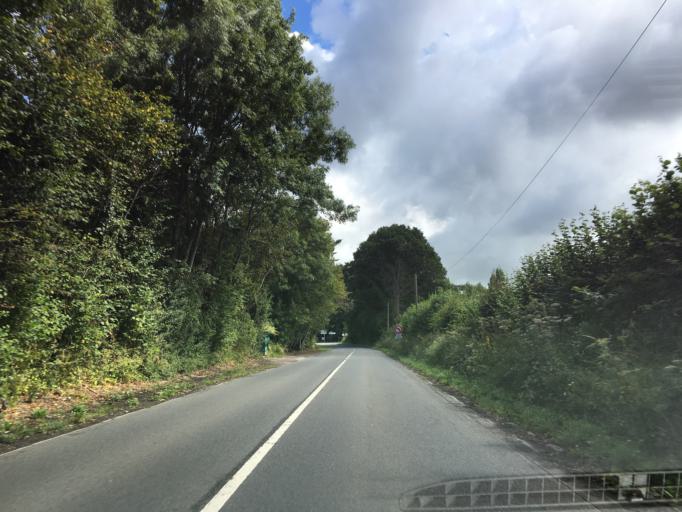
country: FR
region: Lower Normandy
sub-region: Departement du Calvados
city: Dozule
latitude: 49.2706
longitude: -0.0433
